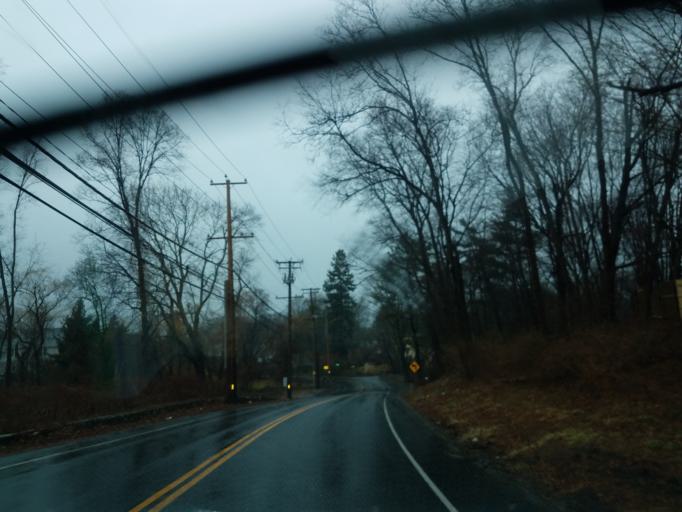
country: US
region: Connecticut
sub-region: Fairfield County
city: Westport
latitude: 41.1266
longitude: -73.3290
